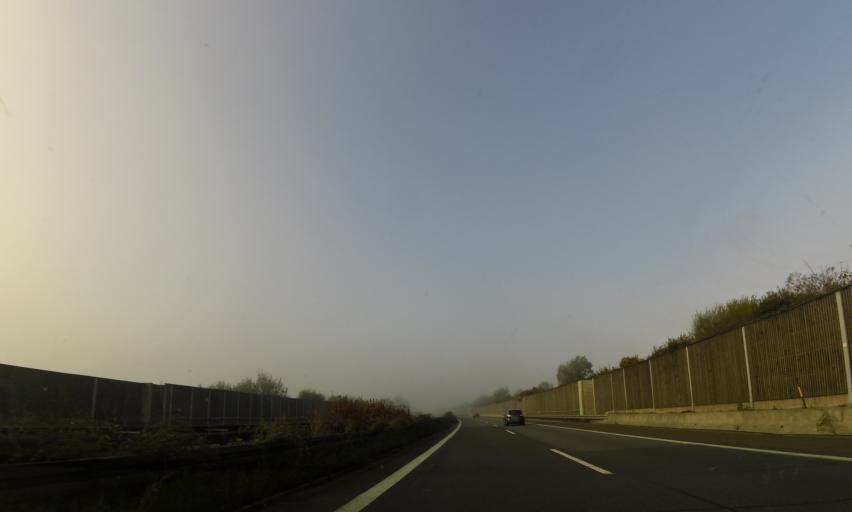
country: DE
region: Saxony
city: Limbach
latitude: 50.5400
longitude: 12.2579
